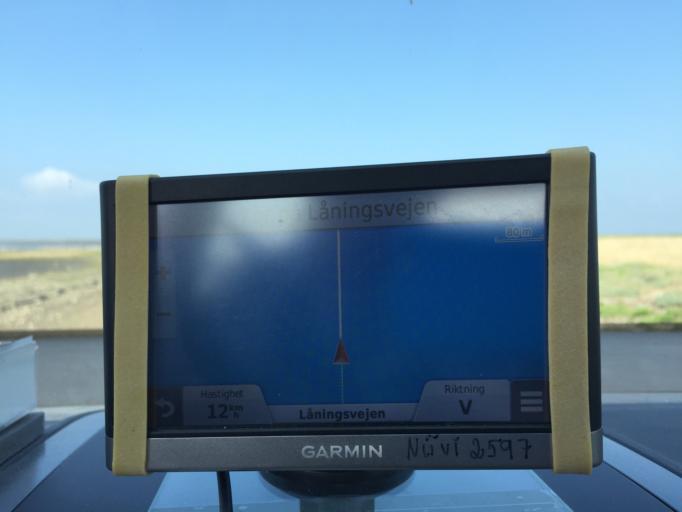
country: DK
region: South Denmark
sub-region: Esbjerg Kommune
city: Ribe
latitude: 55.3079
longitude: 8.6529
